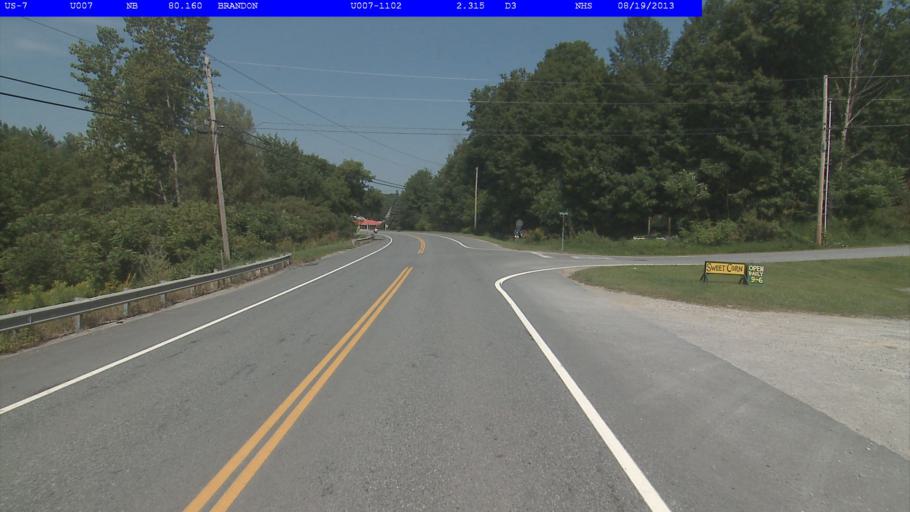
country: US
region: Vermont
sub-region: Rutland County
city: Brandon
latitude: 43.7843
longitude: -73.0644
